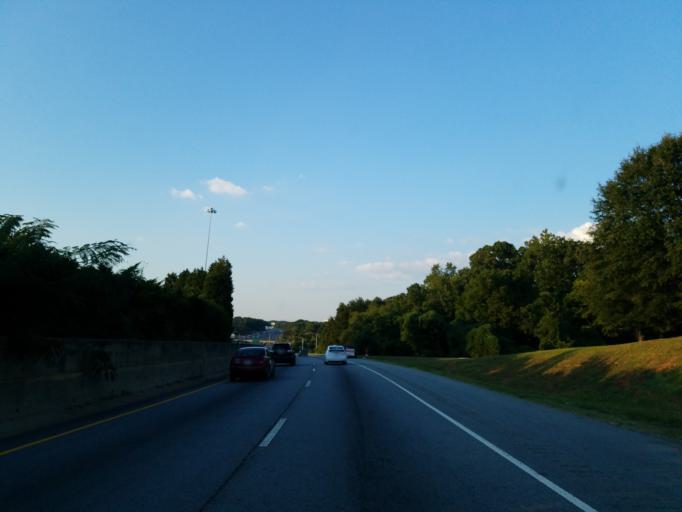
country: US
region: Georgia
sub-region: Fulton County
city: Hapeville
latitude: 33.6976
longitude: -84.4037
